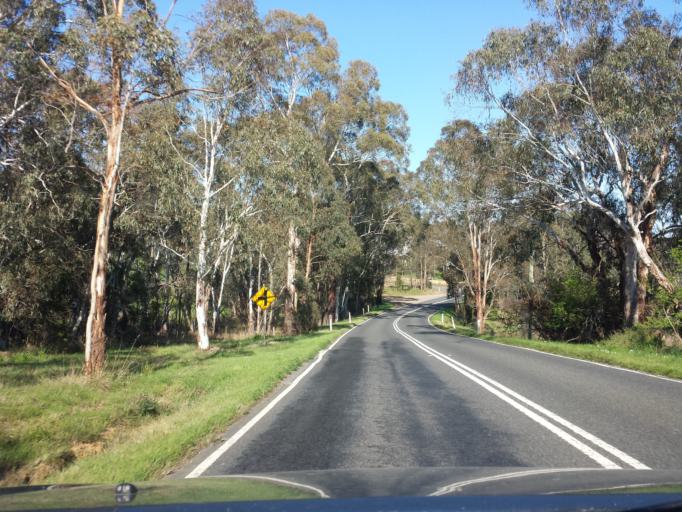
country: AU
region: Victoria
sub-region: Yarra Ranges
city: Yarra Glen
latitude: -37.6502
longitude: 145.3196
